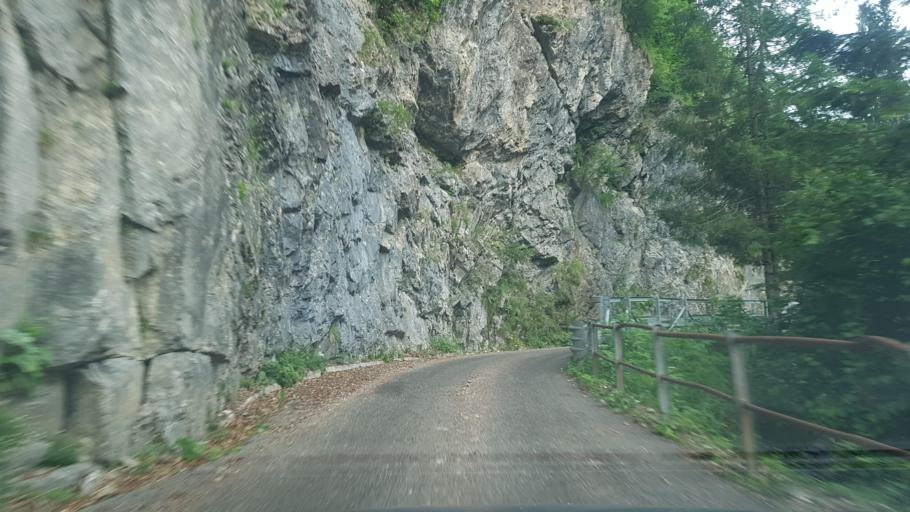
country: IT
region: Friuli Venezia Giulia
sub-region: Provincia di Udine
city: Paularo
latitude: 46.5741
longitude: 13.1115
